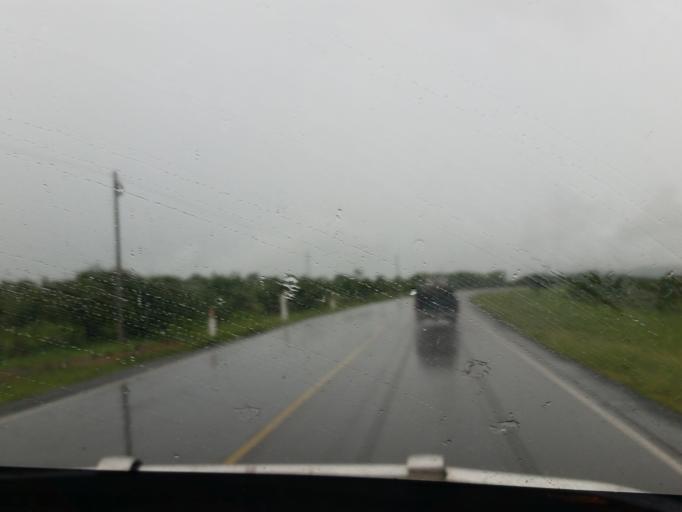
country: NI
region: Matagalpa
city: Ciudad Dario
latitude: 12.7193
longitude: -86.0981
